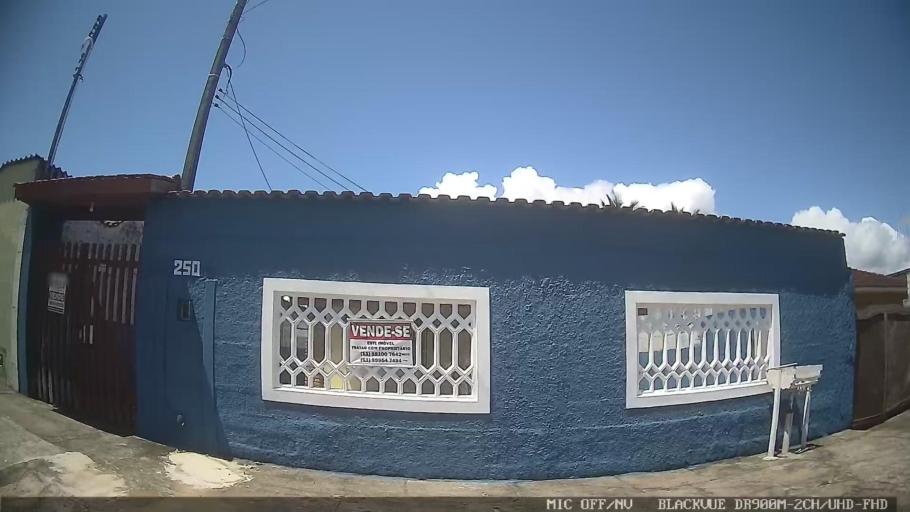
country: BR
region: Sao Paulo
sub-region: Caraguatatuba
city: Caraguatatuba
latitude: -23.6882
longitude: -45.4357
